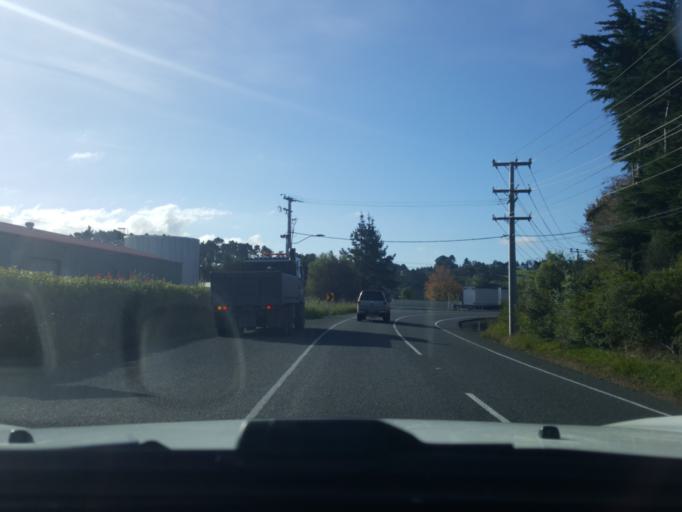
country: NZ
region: Auckland
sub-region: Auckland
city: Muriwai Beach
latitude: -36.7636
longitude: 174.5769
